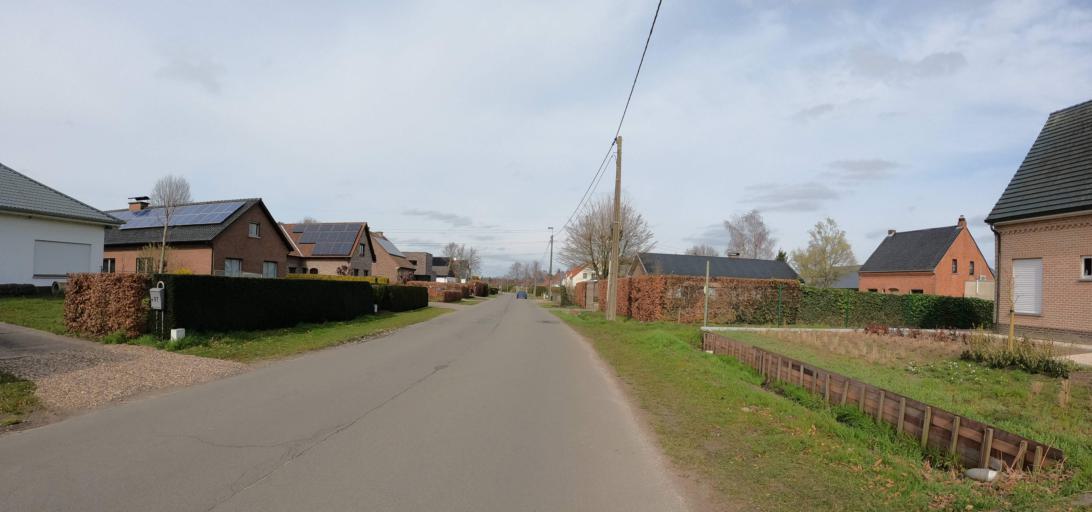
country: BE
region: Flanders
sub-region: Provincie Oost-Vlaanderen
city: Waasmunster
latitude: 51.1354
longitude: 4.0803
